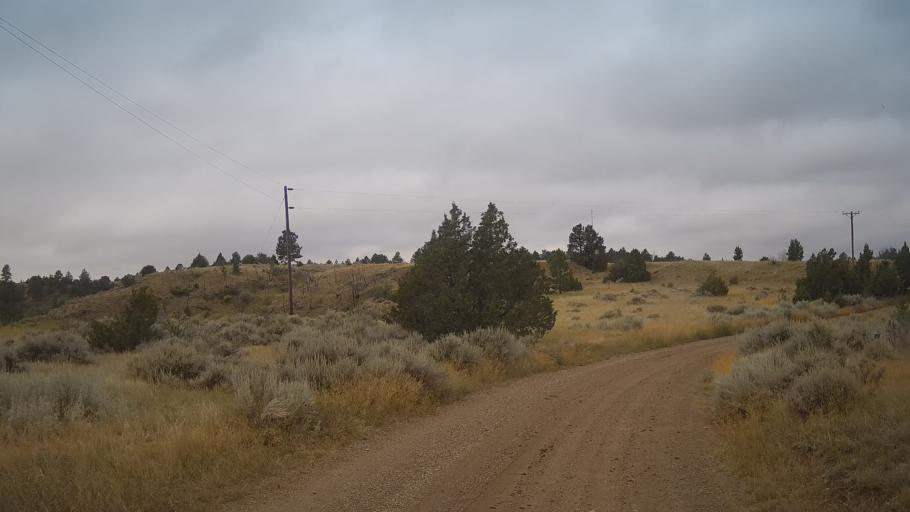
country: US
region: Montana
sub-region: Dawson County
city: Glendive
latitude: 47.0429
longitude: -104.6747
